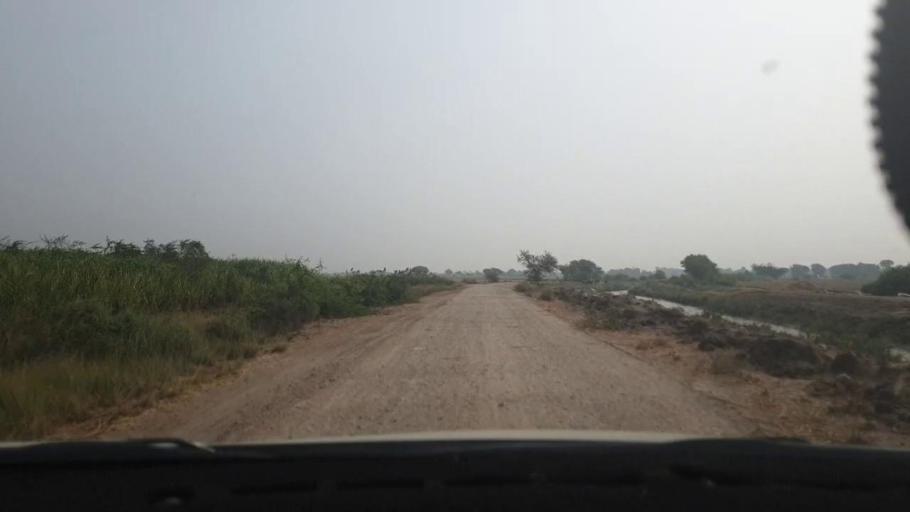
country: PK
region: Sindh
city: Tando Muhammad Khan
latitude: 25.0675
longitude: 68.5057
